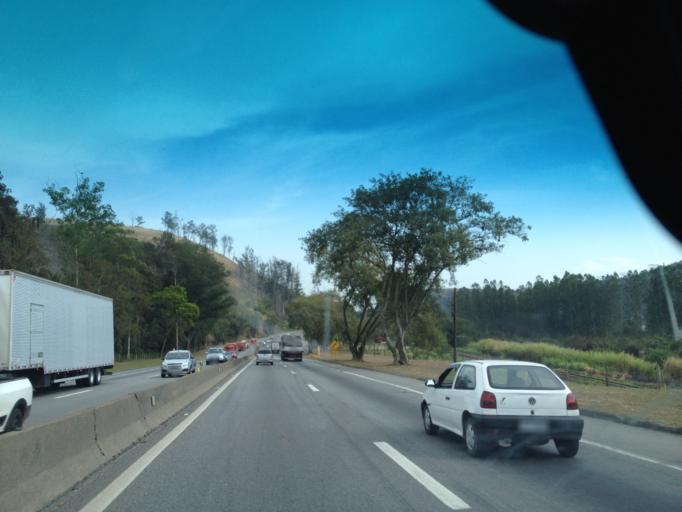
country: BR
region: Rio de Janeiro
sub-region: Barra Mansa
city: Barra Mansa
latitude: -22.4956
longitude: -44.2392
